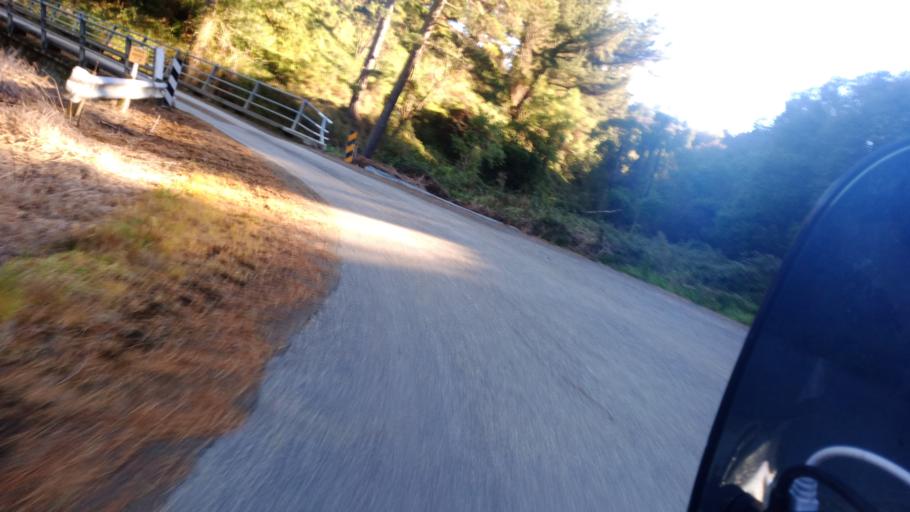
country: NZ
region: Hawke's Bay
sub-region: Wairoa District
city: Wairoa
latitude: -38.8160
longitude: 177.2944
